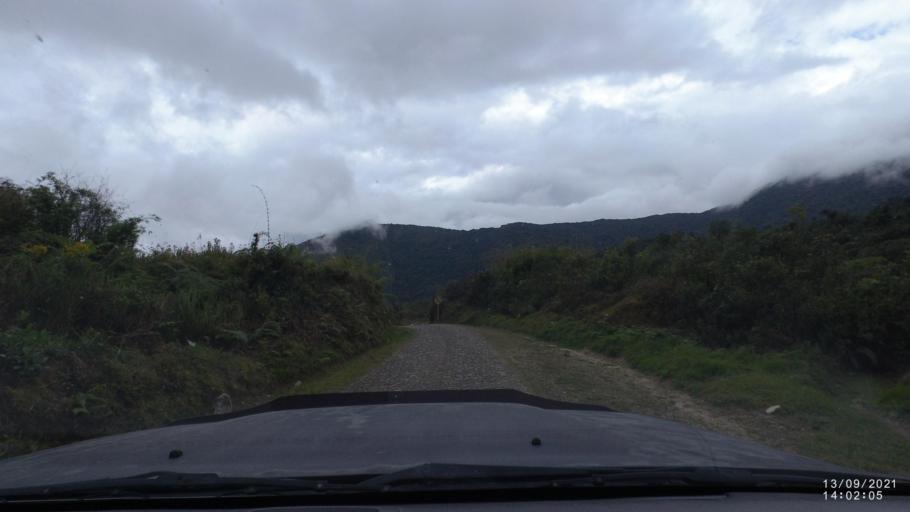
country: BO
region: Cochabamba
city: Colomi
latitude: -17.2096
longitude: -65.8679
